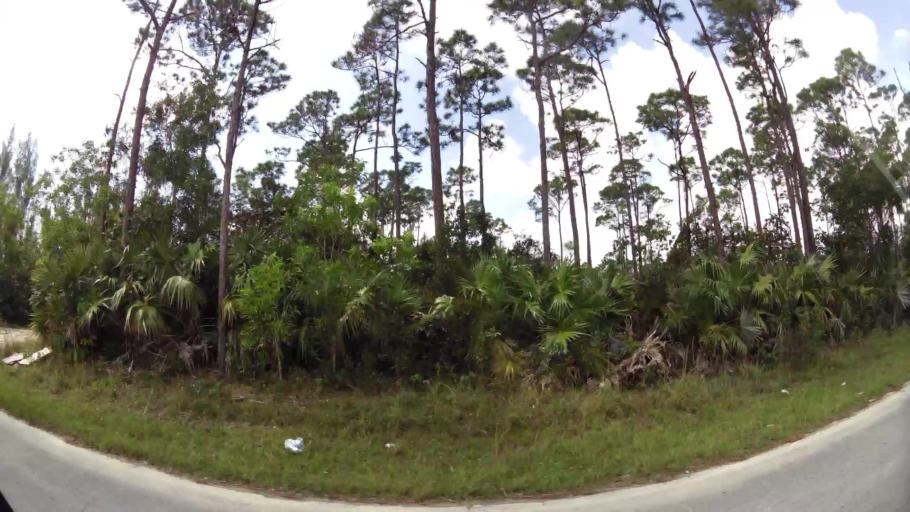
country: BS
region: Freeport
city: Lucaya
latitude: 26.5283
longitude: -78.6569
